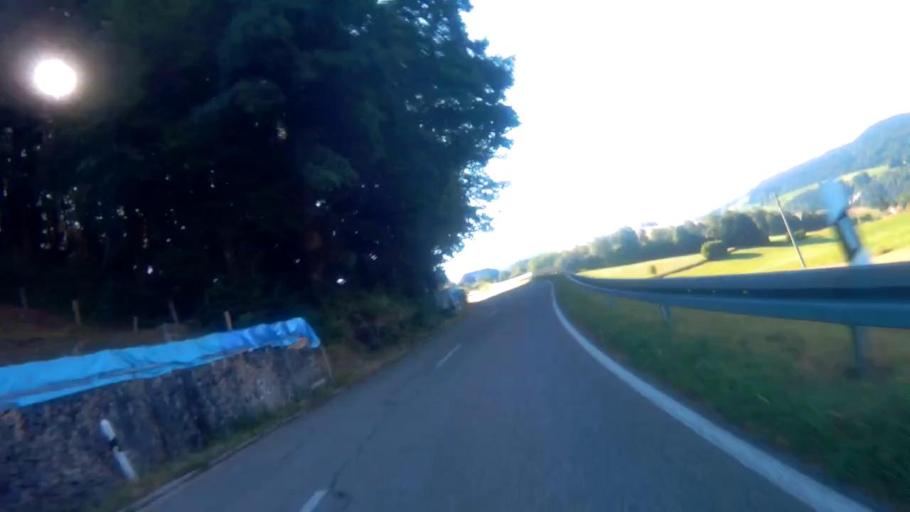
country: DE
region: Baden-Wuerttemberg
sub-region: Freiburg Region
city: Wembach
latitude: 47.7658
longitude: 7.8931
